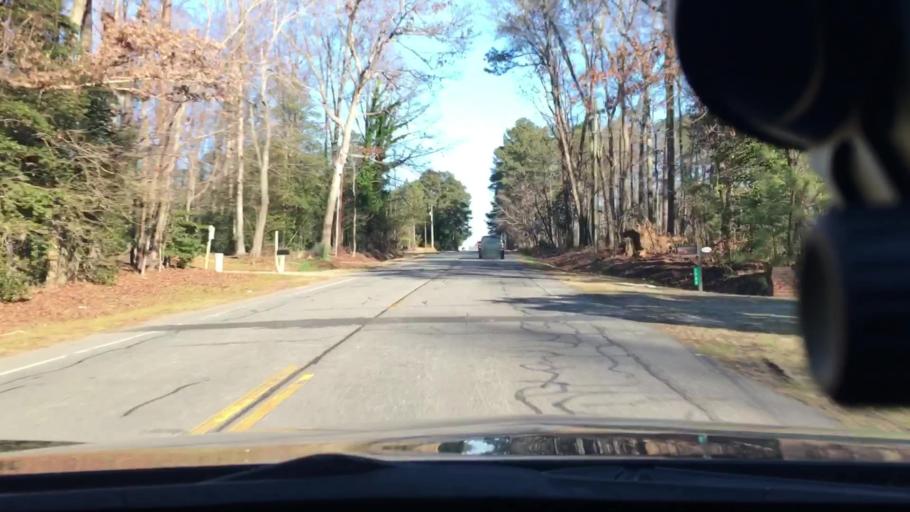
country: US
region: North Carolina
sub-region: Moore County
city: Carthage
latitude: 35.3574
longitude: -79.3364
